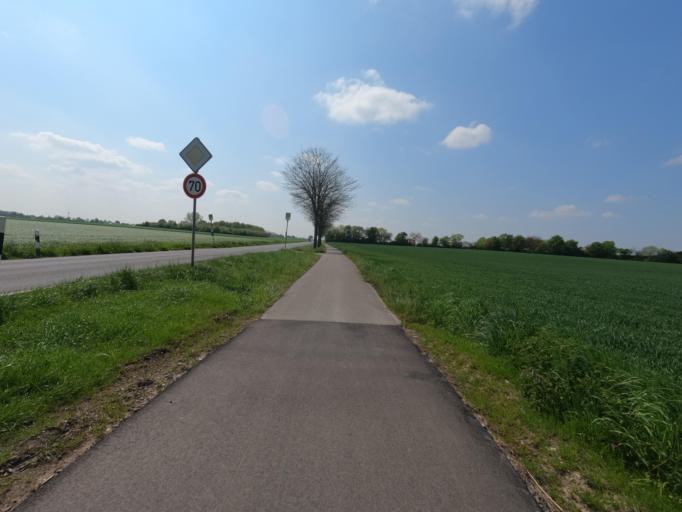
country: DE
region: North Rhine-Westphalia
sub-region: Regierungsbezirk Koln
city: Heinsberg
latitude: 51.0279
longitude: 6.0994
